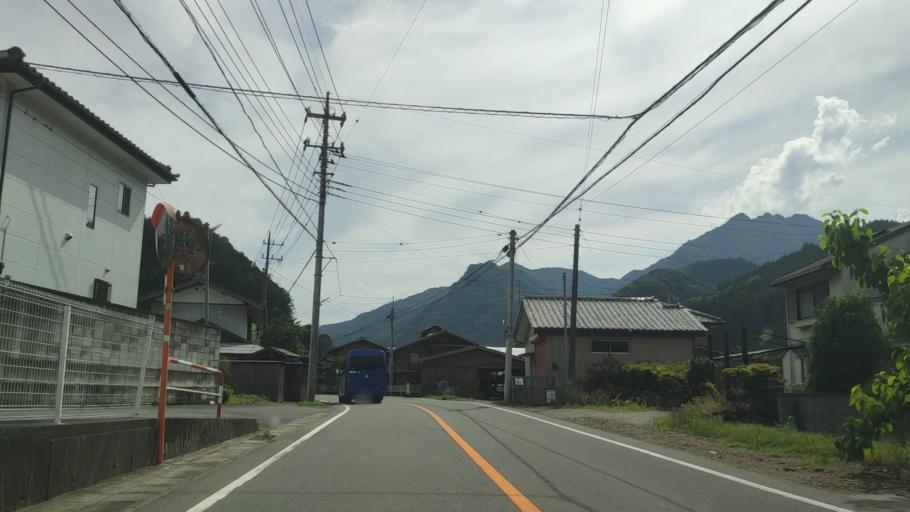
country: JP
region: Gunma
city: Tomioka
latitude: 36.2025
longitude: 138.7667
